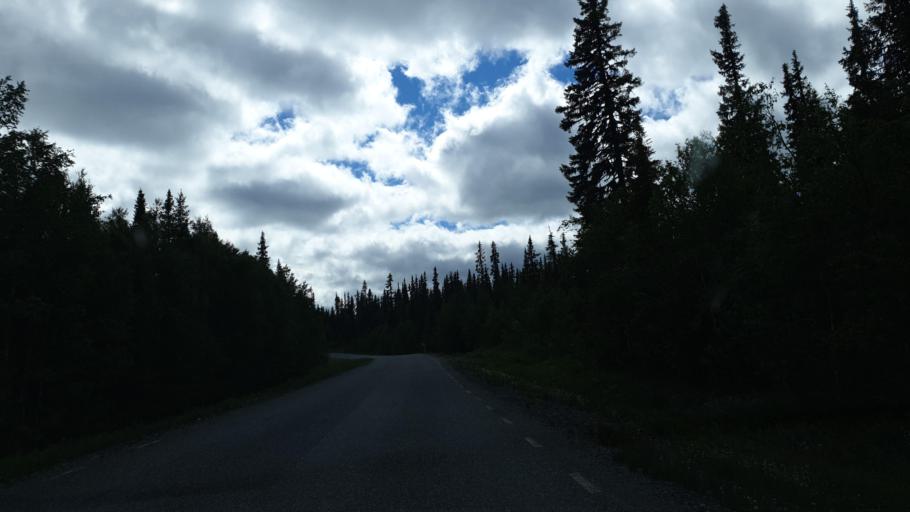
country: SE
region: Vaesterbotten
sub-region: Vilhelmina Kommun
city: Sjoberg
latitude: 65.1254
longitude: 15.8750
